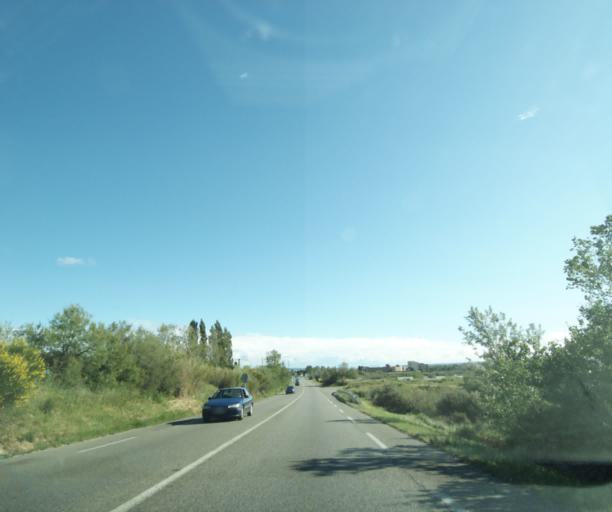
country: FR
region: Provence-Alpes-Cote d'Azur
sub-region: Departement des Bouches-du-Rhone
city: Vitrolles
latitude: 43.4529
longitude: 5.2315
